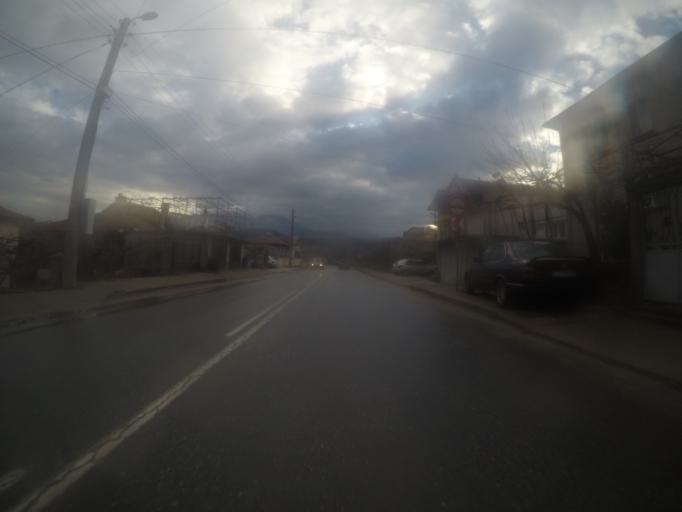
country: BG
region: Blagoevgrad
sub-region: Obshtina Simitli
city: Simitli
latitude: 41.8796
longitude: 23.1267
